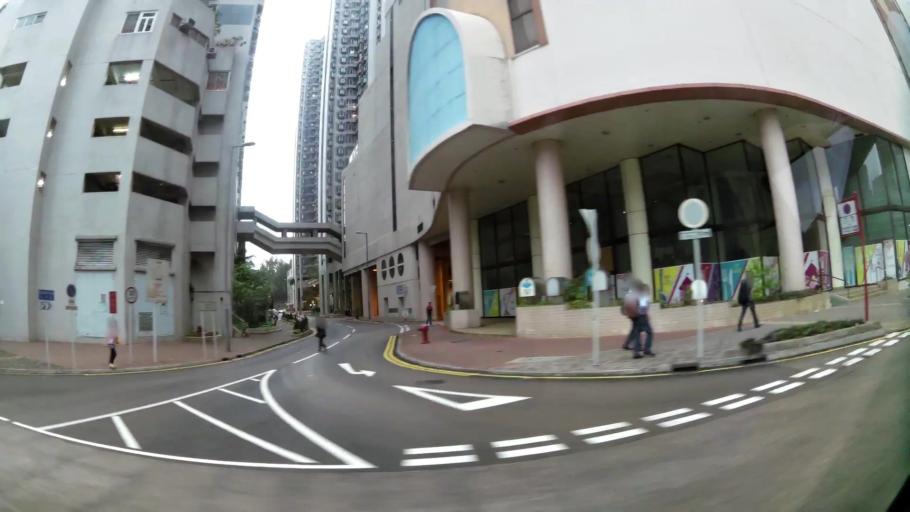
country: HK
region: Tsuen Wan
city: Tsuen Wan
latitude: 22.3630
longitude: 114.1147
